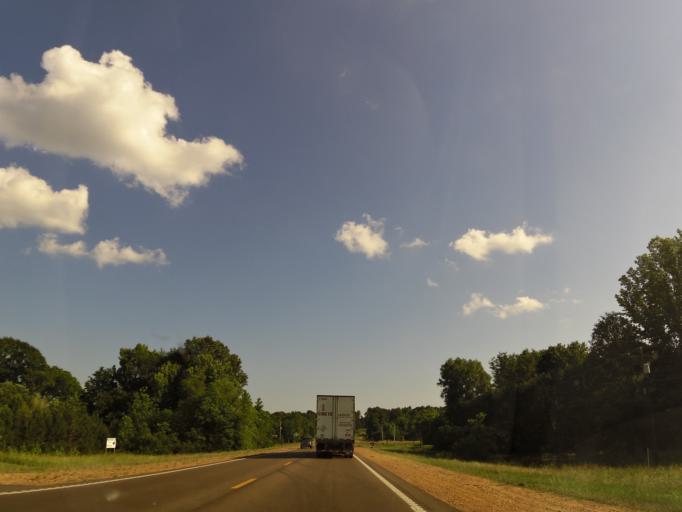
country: US
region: Mississippi
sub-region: Lafayette County
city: University
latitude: 34.3085
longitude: -89.5199
